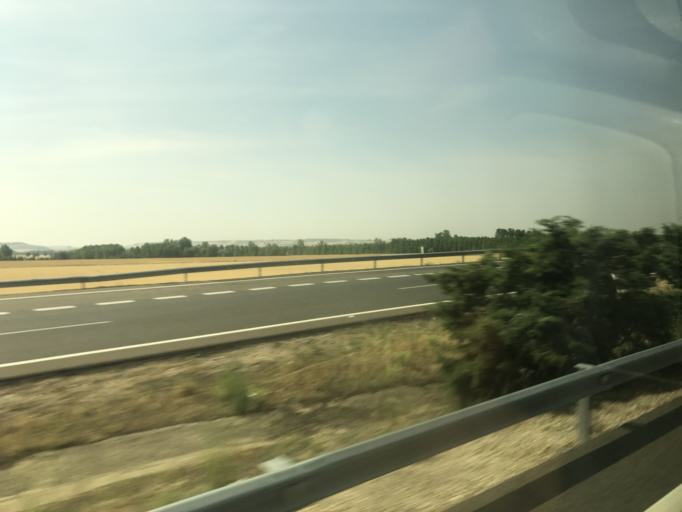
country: ES
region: Castille and Leon
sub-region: Provincia de Palencia
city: Palenzuela
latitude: 42.1183
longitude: -4.1531
